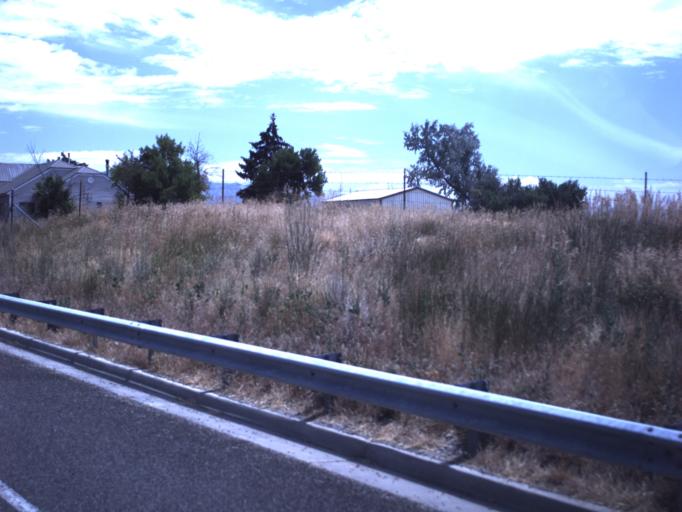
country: US
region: Utah
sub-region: Box Elder County
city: Tremonton
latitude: 41.7103
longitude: -112.2271
